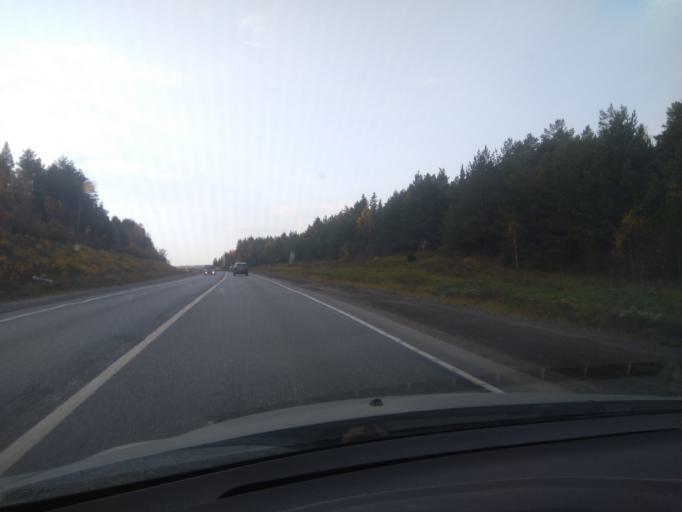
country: RU
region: Sverdlovsk
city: Druzhinino
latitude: 56.8189
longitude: 59.5659
